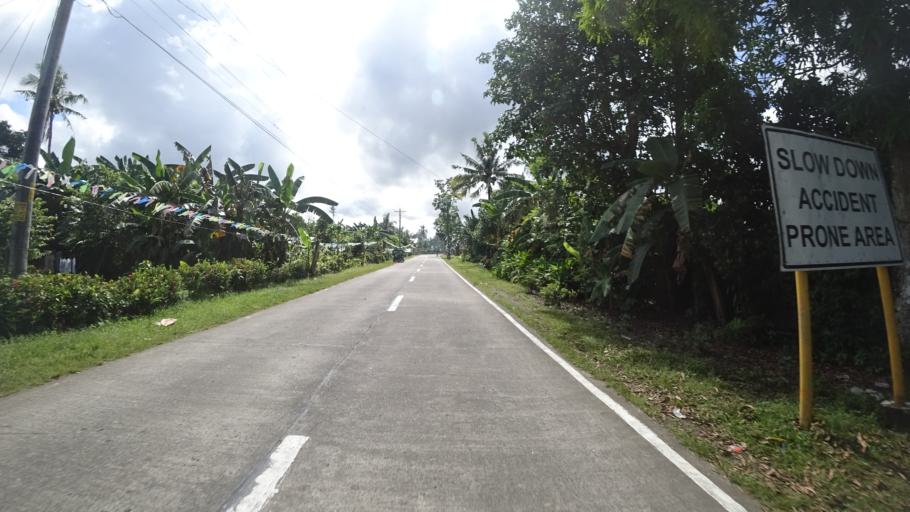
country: PH
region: Eastern Visayas
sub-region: Province of Leyte
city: Burauen
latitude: 10.9807
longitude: 124.9206
